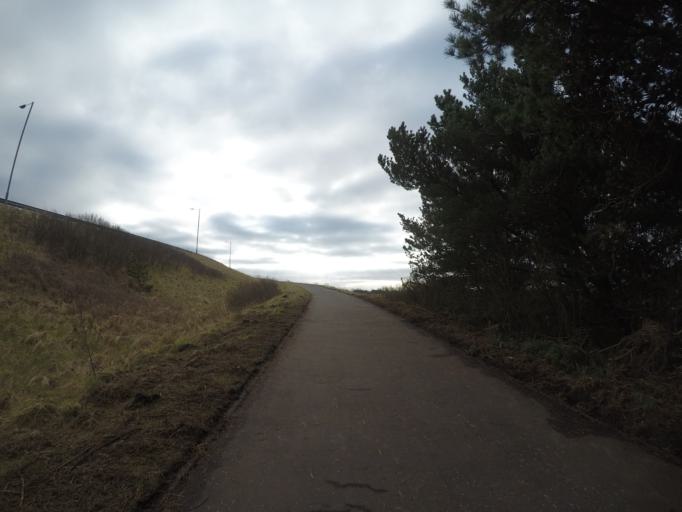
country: GB
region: Scotland
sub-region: North Ayrshire
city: Irvine
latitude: 55.5905
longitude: -4.6679
